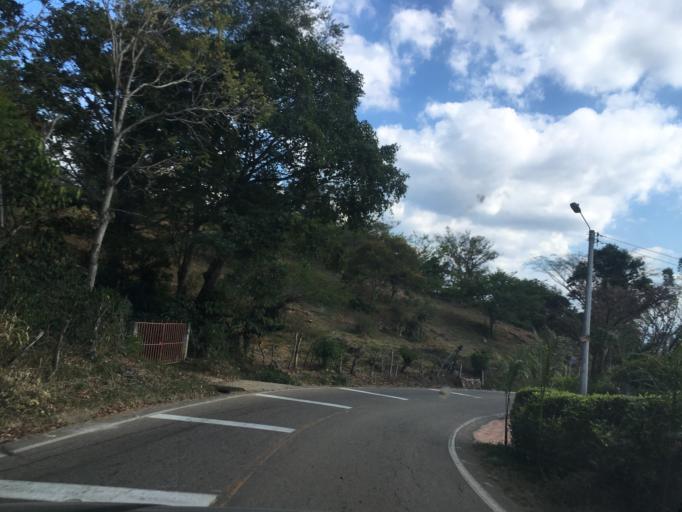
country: CO
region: Santander
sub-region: San Gil
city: San Gil
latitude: 6.5798
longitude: -73.1557
